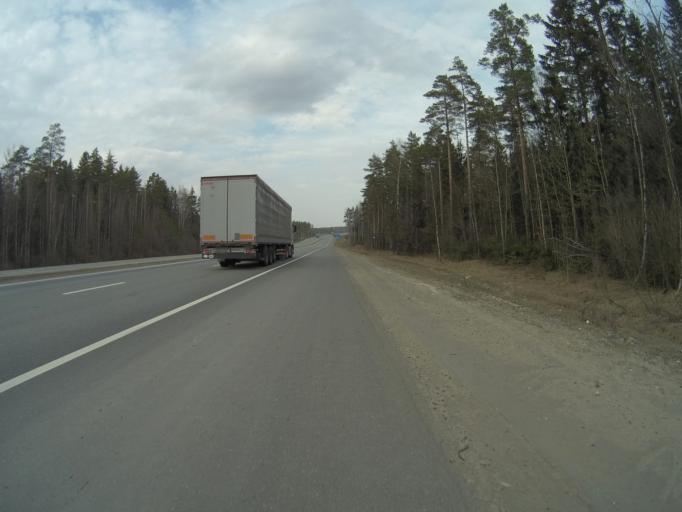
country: RU
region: Vladimir
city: Kommunar
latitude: 56.0713
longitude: 40.4648
